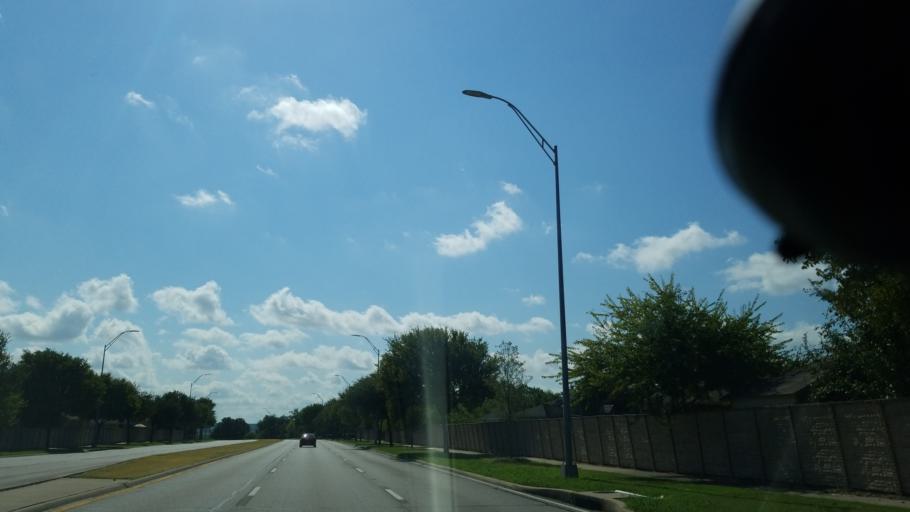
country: US
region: Texas
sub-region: Dallas County
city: Grand Prairie
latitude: 32.7072
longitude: -96.9897
